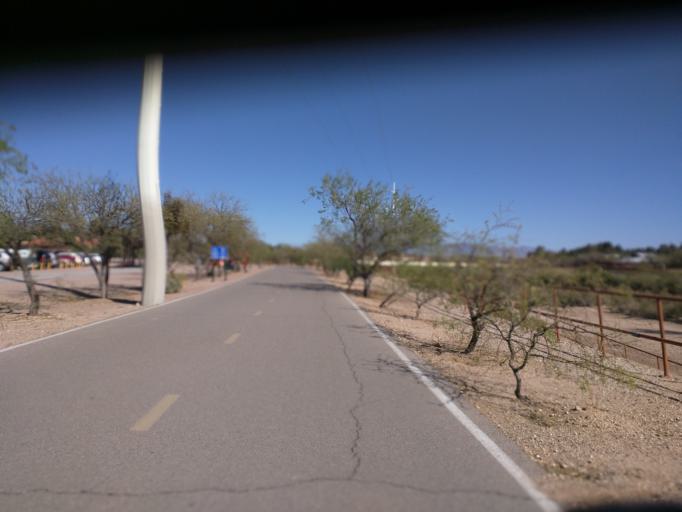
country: US
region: Arizona
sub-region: Pima County
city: Catalina Foothills
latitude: 32.2880
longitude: -110.9546
